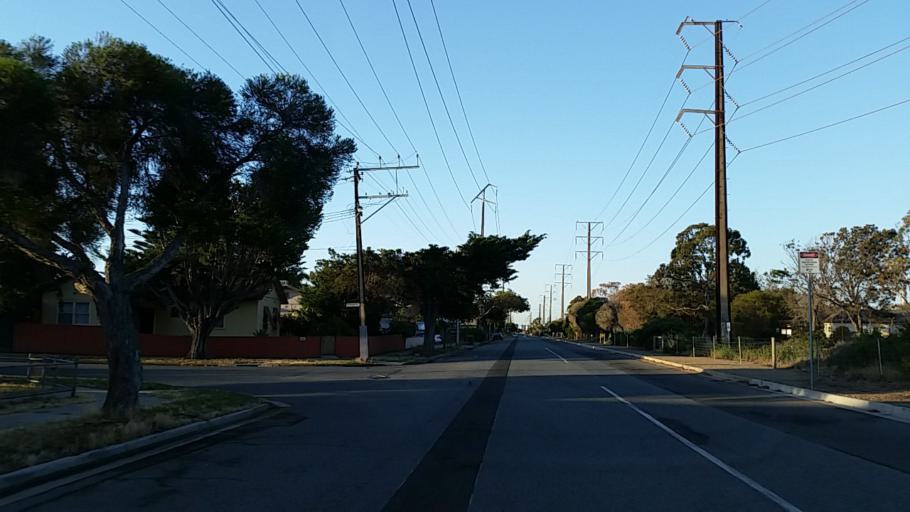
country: AU
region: South Australia
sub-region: Port Adelaide Enfield
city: Birkenhead
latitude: -34.8028
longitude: 138.5050
